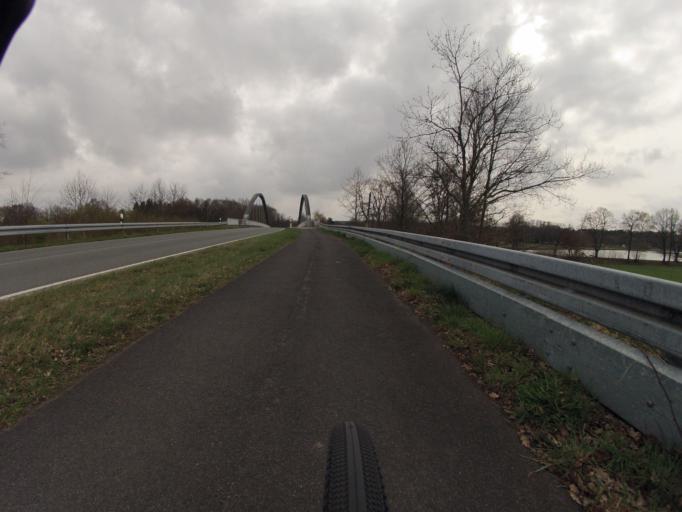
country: DE
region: North Rhine-Westphalia
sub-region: Regierungsbezirk Munster
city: Recke
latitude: 52.3565
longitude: 7.7160
